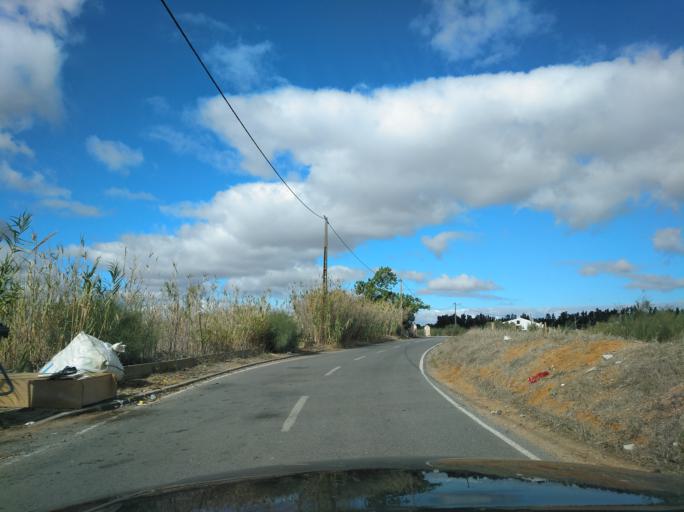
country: PT
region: Faro
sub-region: Vila Real de Santo Antonio
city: Monte Gordo
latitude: 37.1826
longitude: -7.4951
